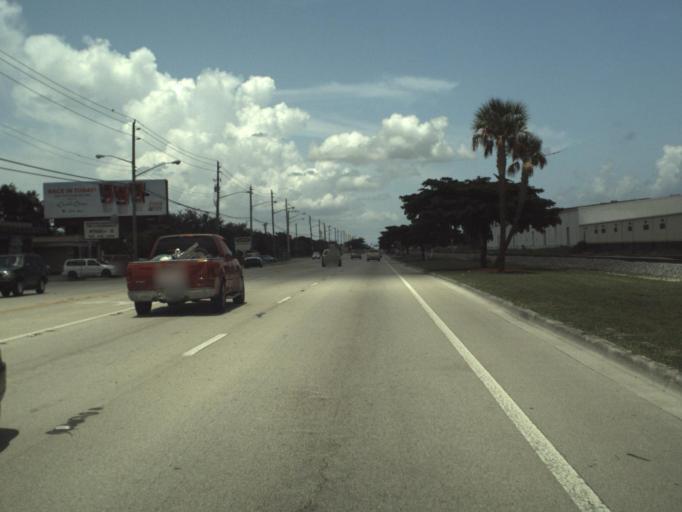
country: US
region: Florida
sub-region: Broward County
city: Kendall Green
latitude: 26.2641
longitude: -80.1168
